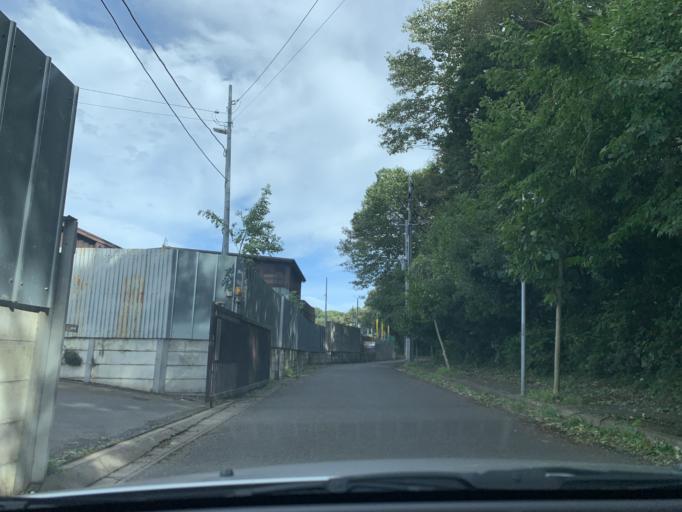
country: JP
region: Chiba
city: Nagareyama
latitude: 35.8980
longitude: 139.8971
